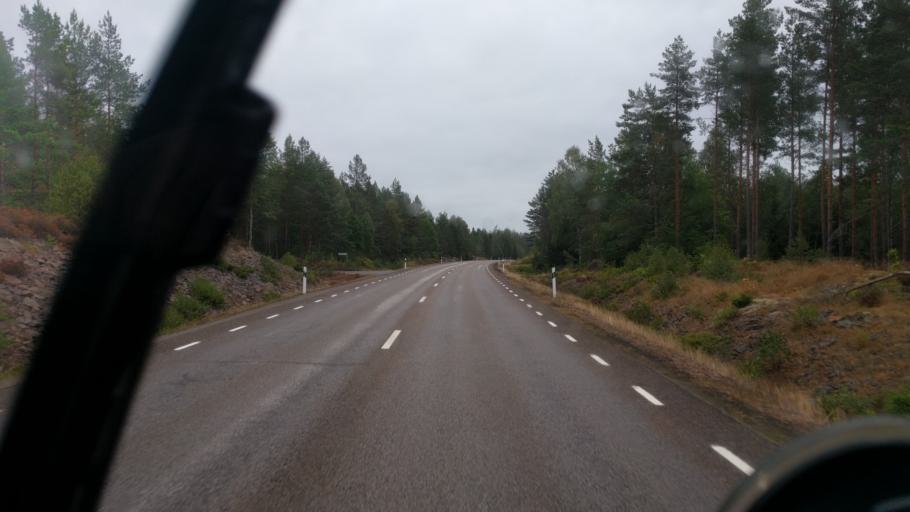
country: SE
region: Kalmar
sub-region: Vasterviks Kommun
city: Ankarsrum
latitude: 57.7048
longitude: 16.2019
